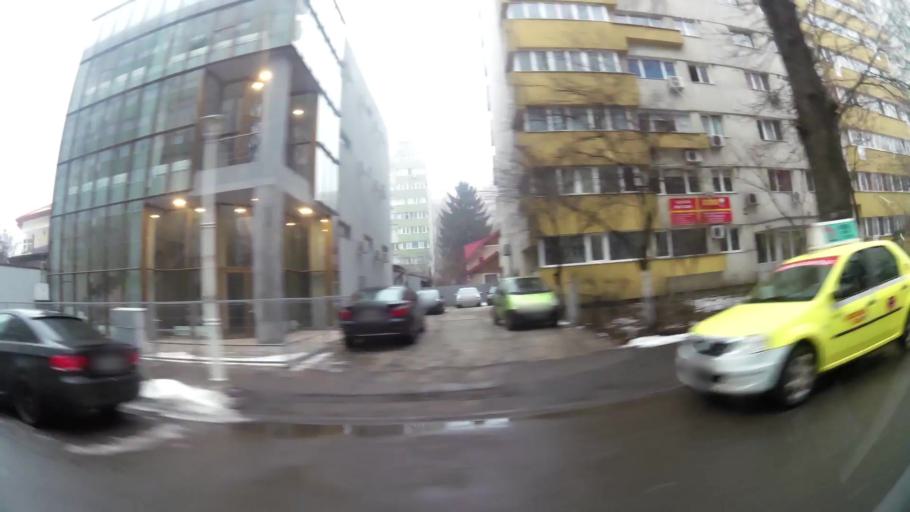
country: RO
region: Ilfov
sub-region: Comuna Chiajna
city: Rosu
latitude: 44.4859
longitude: 26.0370
